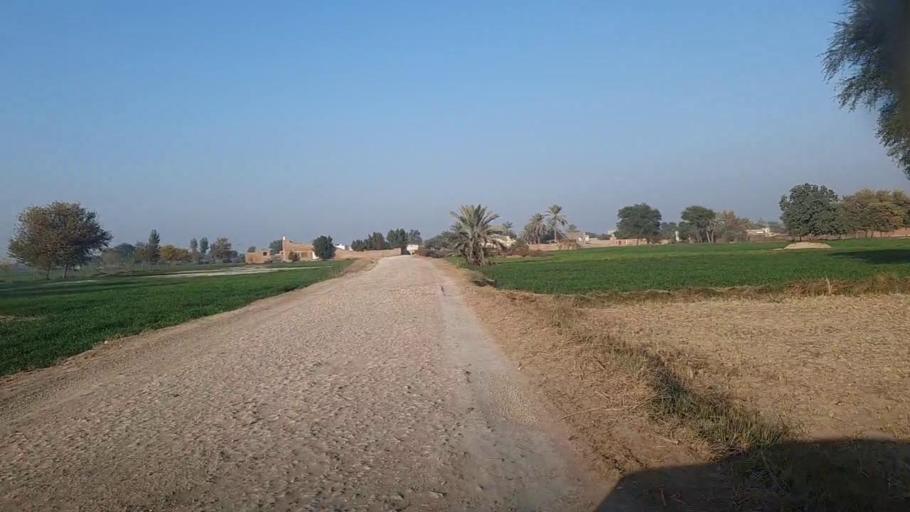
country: PK
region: Sindh
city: Khairpur
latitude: 28.0736
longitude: 69.7445
